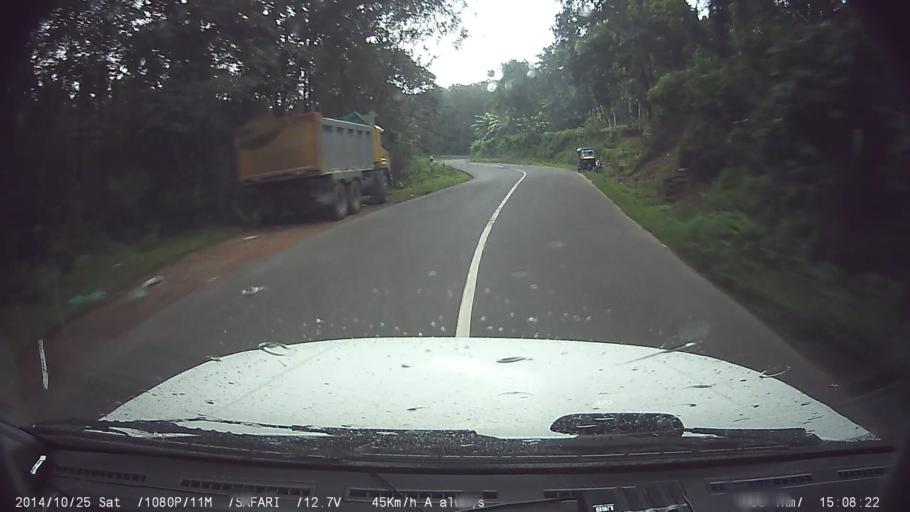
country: IN
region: Kerala
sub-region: Kottayam
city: Palackattumala
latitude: 9.8248
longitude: 76.5859
